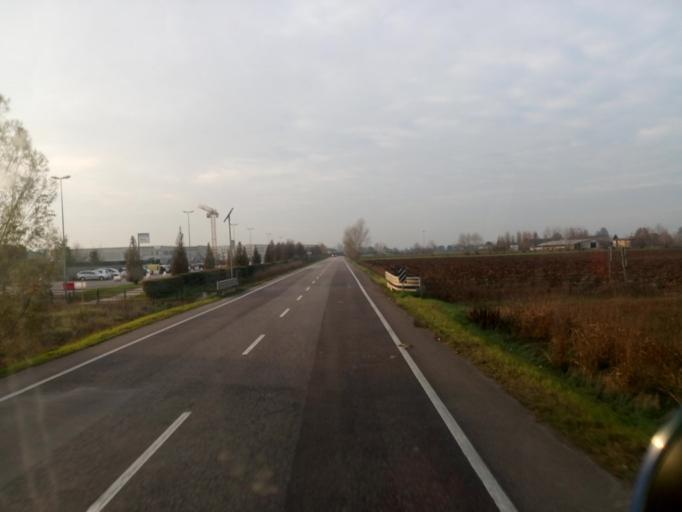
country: IT
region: Veneto
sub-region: Provincia di Verona
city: Pradelle
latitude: 45.2804
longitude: 10.8683
